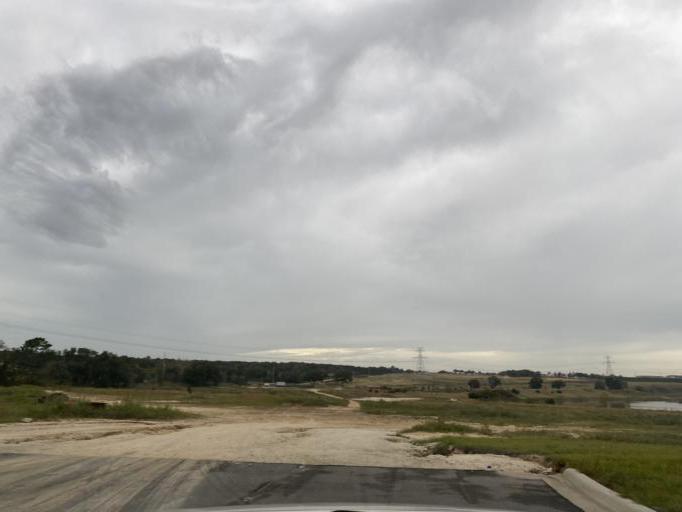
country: US
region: Florida
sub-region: Orange County
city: Oakland
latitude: 28.5299
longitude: -81.6908
